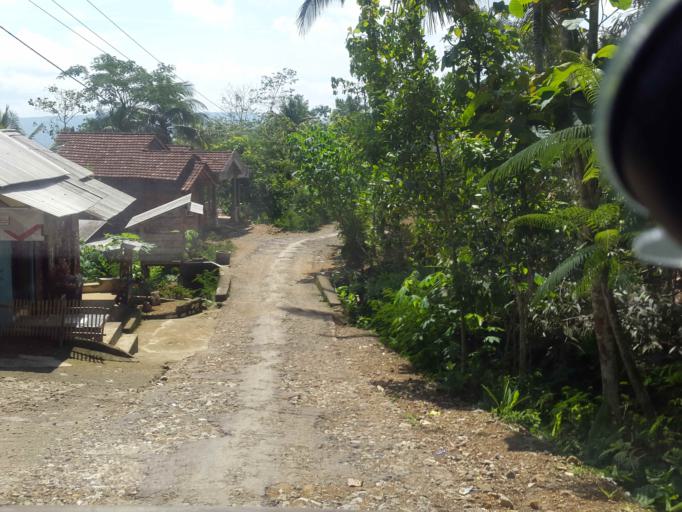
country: ID
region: East Java
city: Sidem
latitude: -8.1072
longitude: 111.5902
